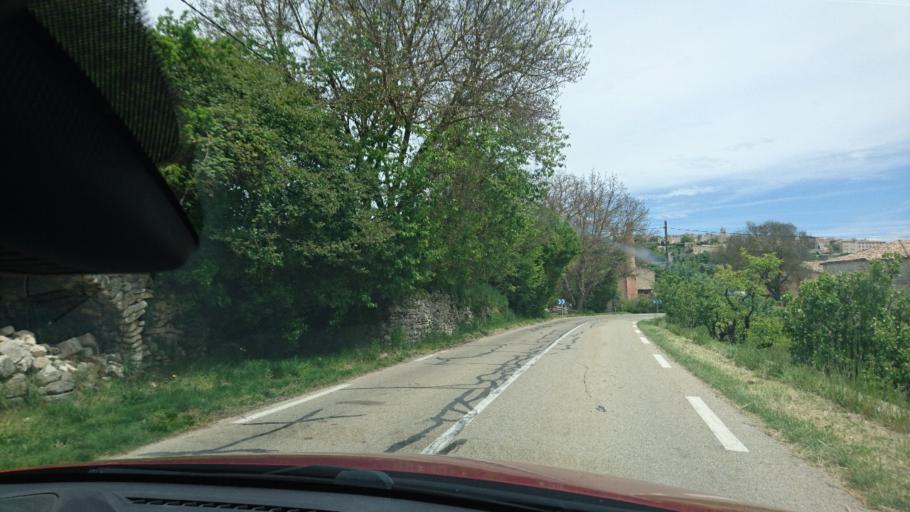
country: FR
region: Provence-Alpes-Cote d'Azur
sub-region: Departement du Vaucluse
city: Sault
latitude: 44.0937
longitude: 5.3983
